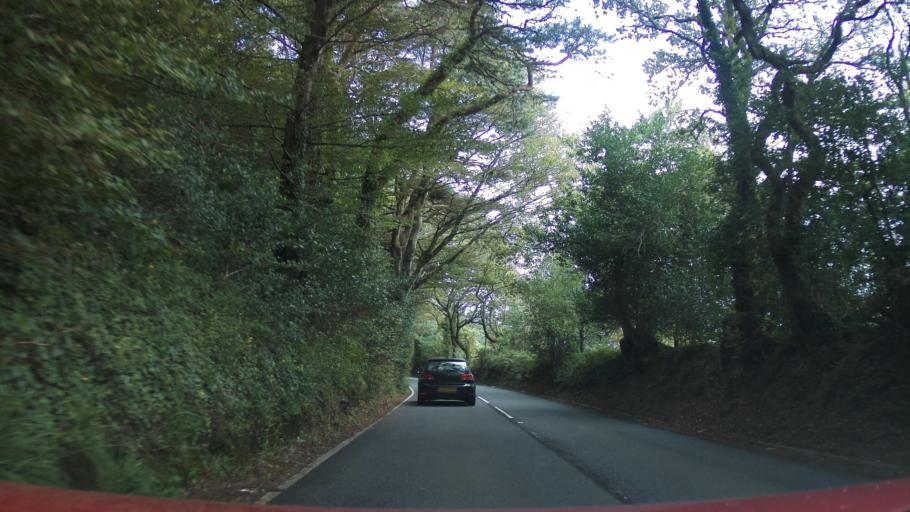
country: GB
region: England
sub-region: Devon
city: Bishopsteignton
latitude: 50.5683
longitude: -3.5158
